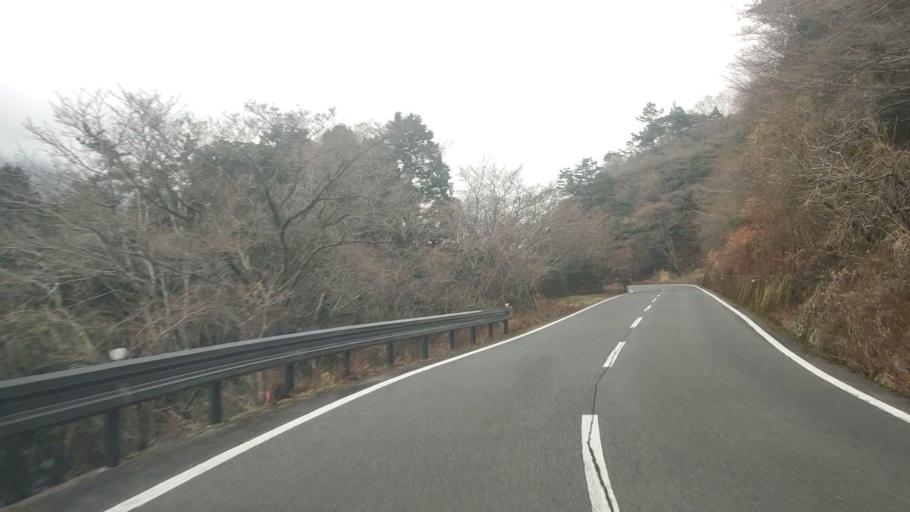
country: JP
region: Nagasaki
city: Shimabara
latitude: 32.7713
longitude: 130.2714
